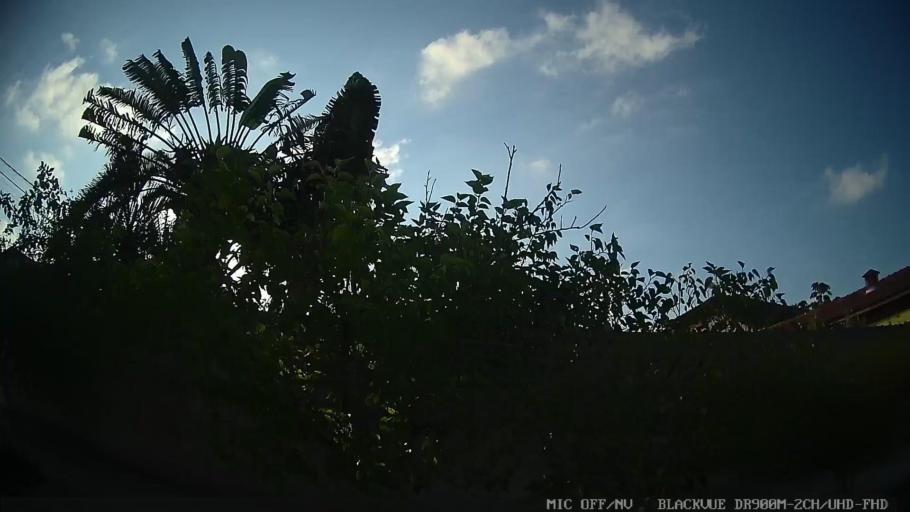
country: BR
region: Sao Paulo
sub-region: Peruibe
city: Peruibe
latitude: -24.2882
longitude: -46.9608
